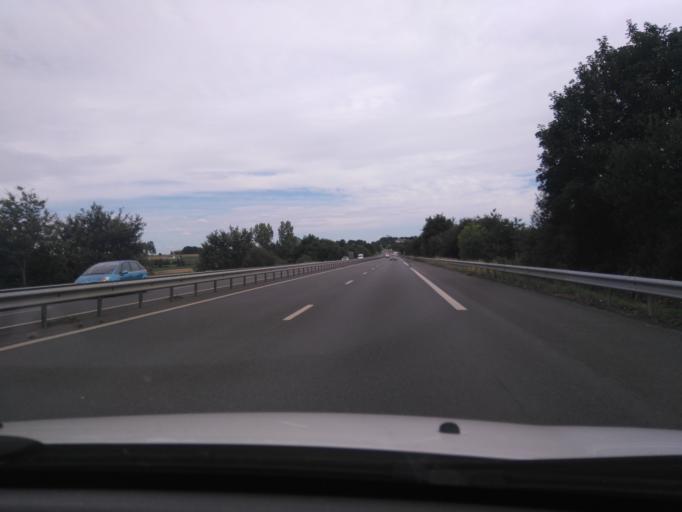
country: FR
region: Brittany
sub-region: Departement des Cotes-d'Armor
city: Broons
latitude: 48.3324
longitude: -2.2655
